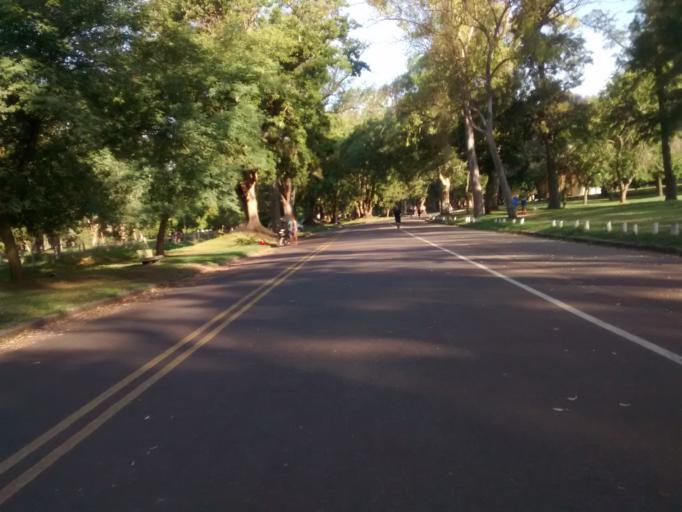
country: AR
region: Buenos Aires
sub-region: Partido de La Plata
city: La Plata
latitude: -34.9073
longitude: -57.9305
